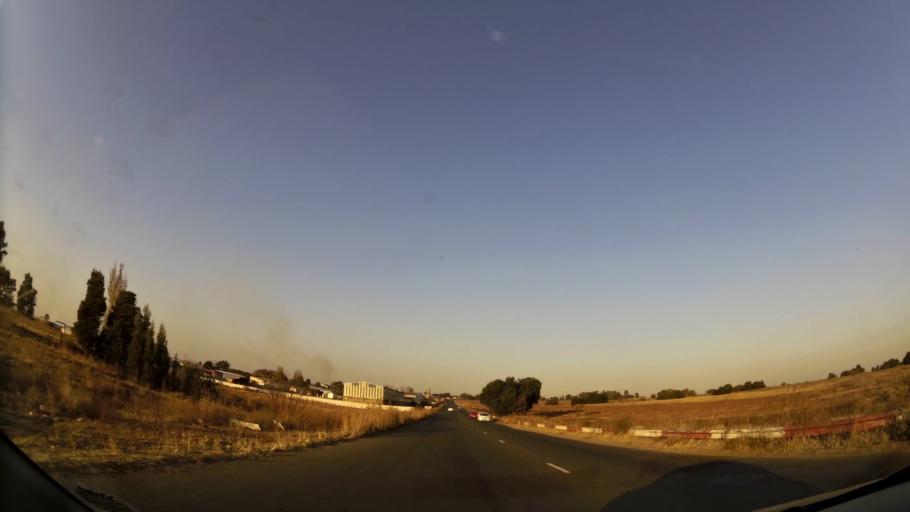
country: ZA
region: Gauteng
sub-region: West Rand District Municipality
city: Randfontein
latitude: -26.2021
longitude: 27.6761
